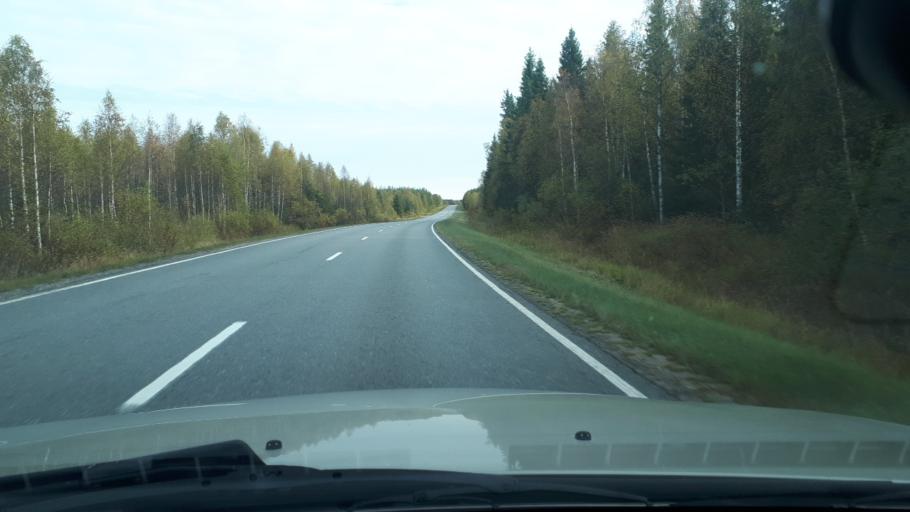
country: FI
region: Lapland
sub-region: Rovaniemi
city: Ranua
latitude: 65.9777
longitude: 26.1232
